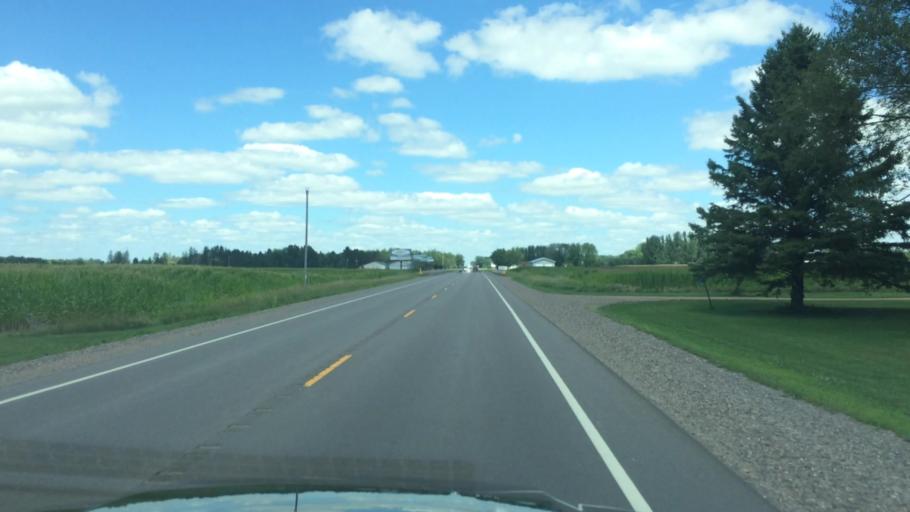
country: US
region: Wisconsin
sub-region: Clark County
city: Abbotsford
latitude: 45.0118
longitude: -90.3153
